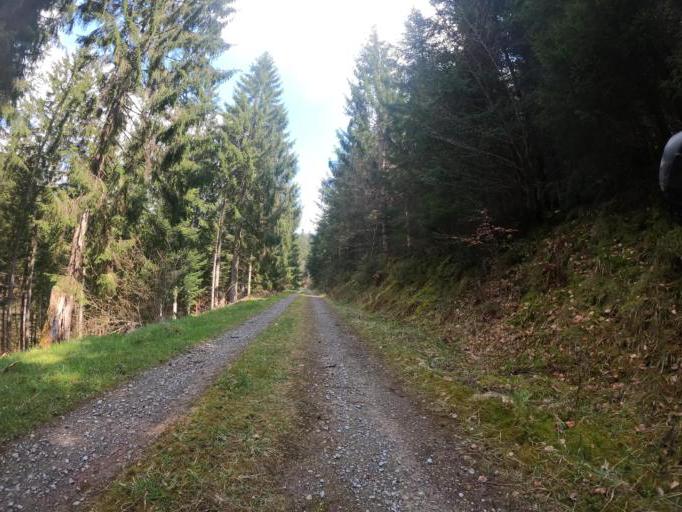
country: DE
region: Baden-Wuerttemberg
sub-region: Karlsruhe Region
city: Schomberg
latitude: 48.7669
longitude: 8.6103
